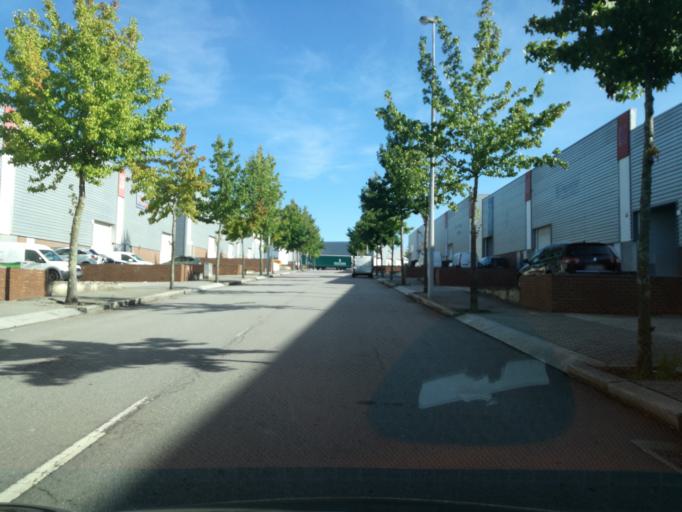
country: PT
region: Porto
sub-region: Maia
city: Anta
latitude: 41.2751
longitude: -8.6049
